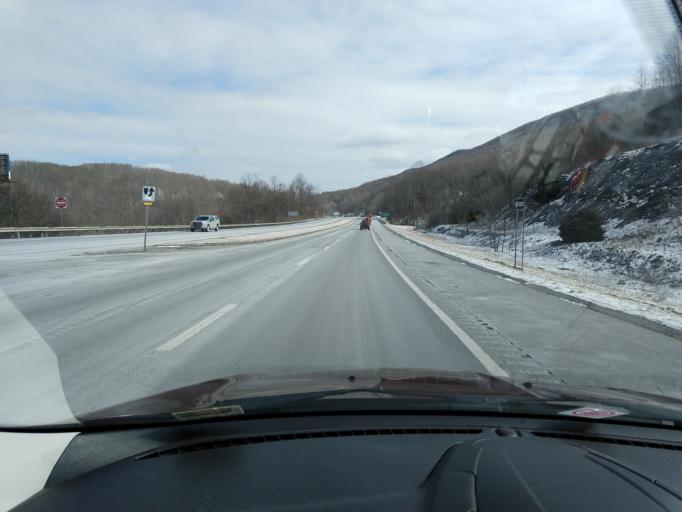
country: US
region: West Virginia
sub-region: Mercer County
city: Bluefield
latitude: 37.2752
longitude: -81.1513
